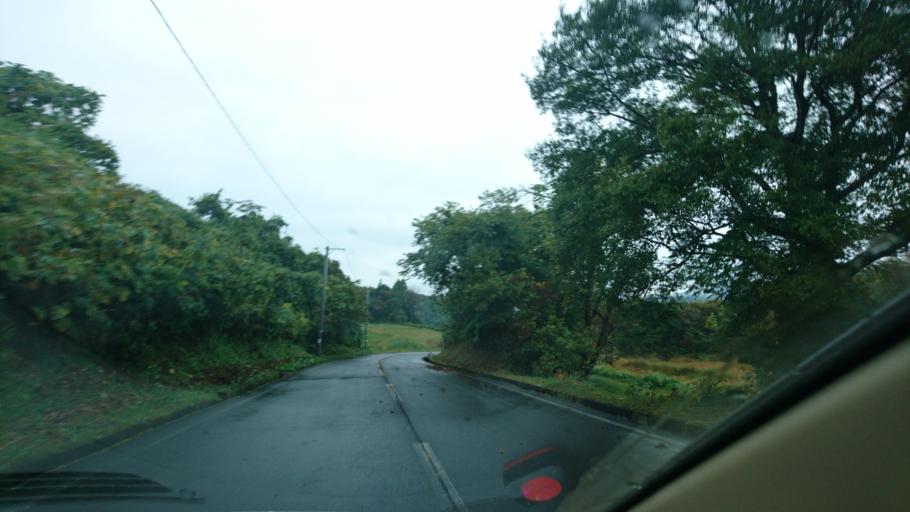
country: JP
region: Iwate
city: Ichinoseki
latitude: 38.9683
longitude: 141.1026
